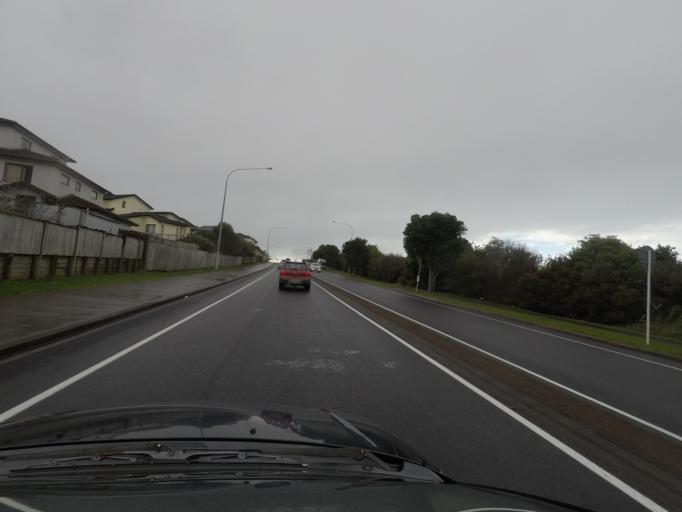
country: NZ
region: Auckland
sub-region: Auckland
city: Rothesay Bay
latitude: -36.7294
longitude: 174.7256
